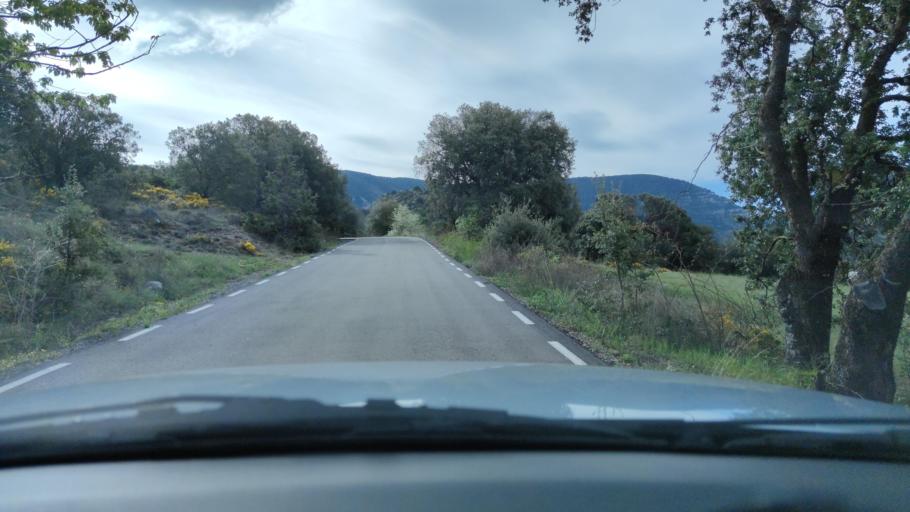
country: ES
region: Catalonia
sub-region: Provincia de Lleida
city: Coll de Nargo
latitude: 42.2324
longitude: 1.3986
